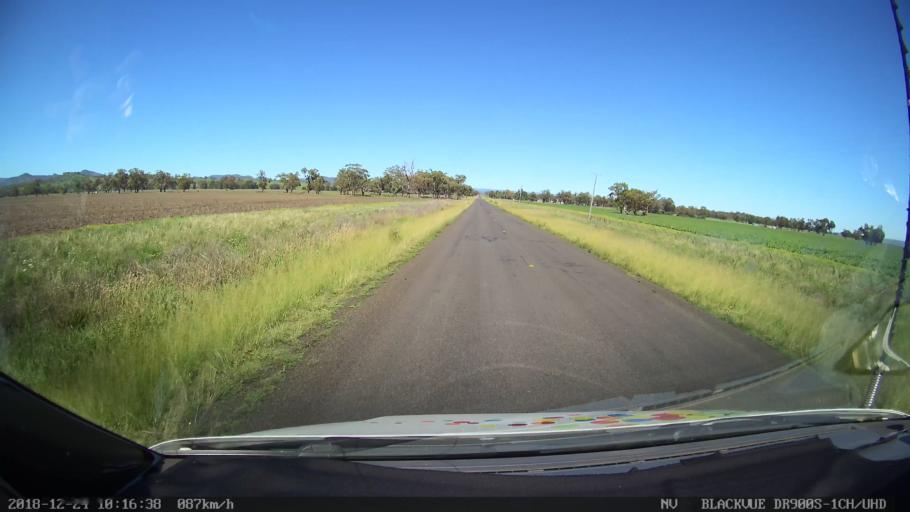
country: AU
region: New South Wales
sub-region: Liverpool Plains
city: Quirindi
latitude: -31.7170
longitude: 150.6033
